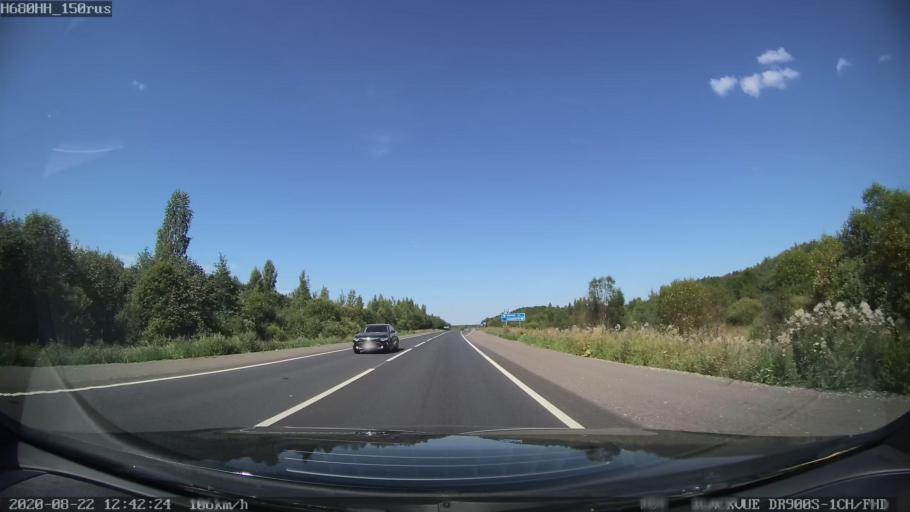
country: RU
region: Tverskaya
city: Rameshki
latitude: 57.3615
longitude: 36.0933
